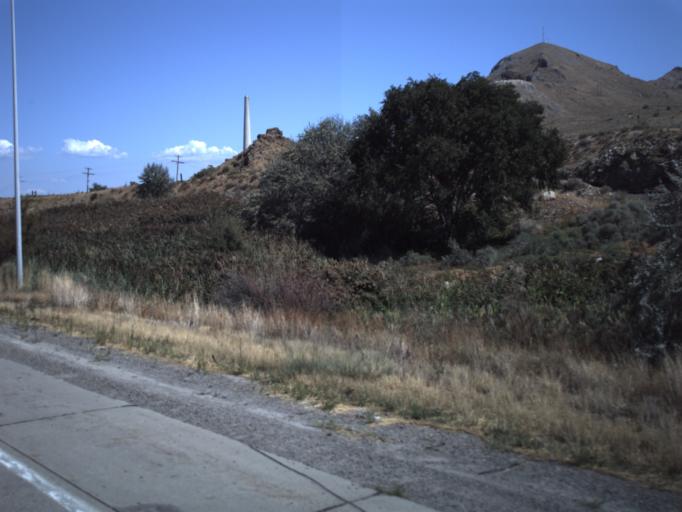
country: US
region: Utah
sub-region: Tooele County
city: Stansbury park
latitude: 40.7209
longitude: -112.2295
